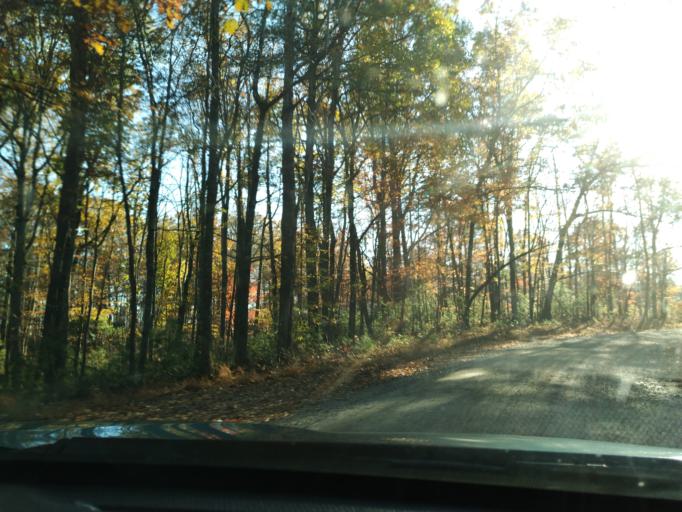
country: US
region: Virginia
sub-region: Floyd County
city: Floyd
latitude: 36.8326
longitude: -80.1975
